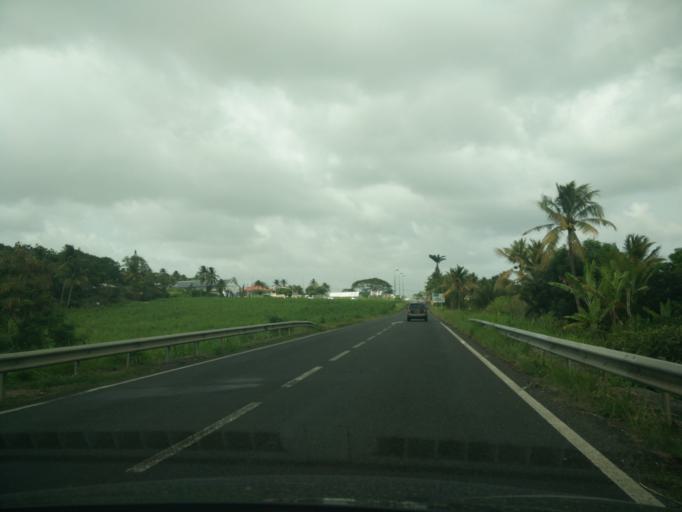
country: GP
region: Guadeloupe
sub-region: Guadeloupe
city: Petit-Bourg
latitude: 16.2177
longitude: -61.6033
